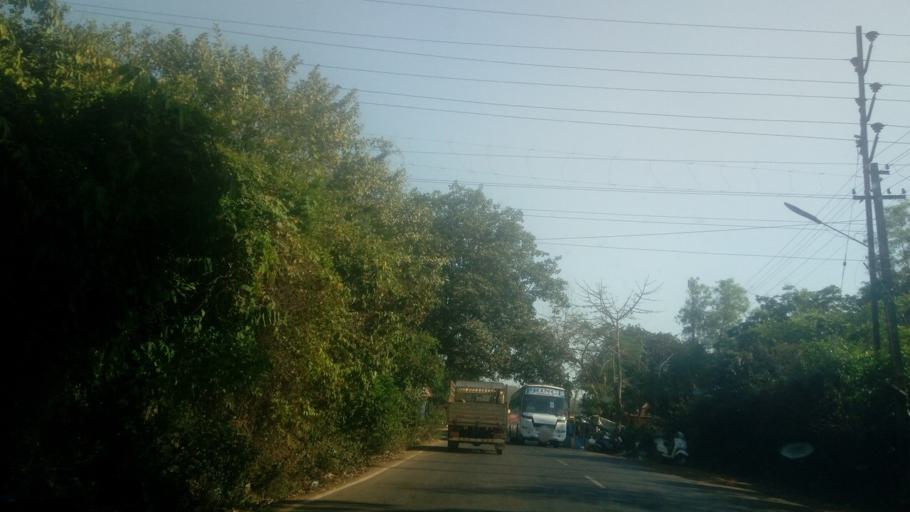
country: IN
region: Goa
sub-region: North Goa
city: Jua
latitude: 15.4912
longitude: 73.9572
